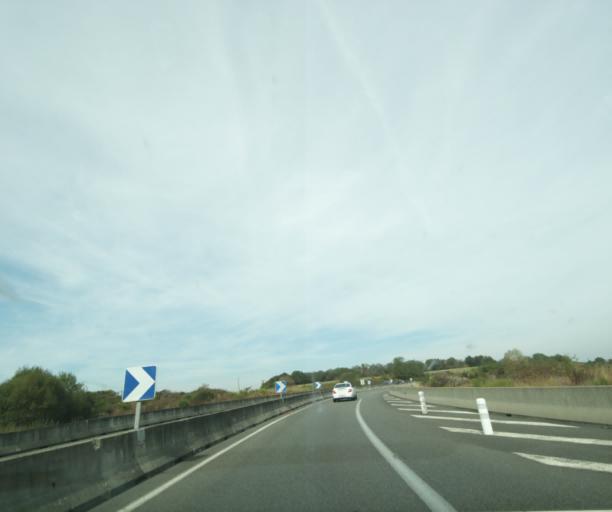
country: FR
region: Auvergne
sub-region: Departement de l'Allier
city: Lapalisse
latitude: 46.2420
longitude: 3.6181
